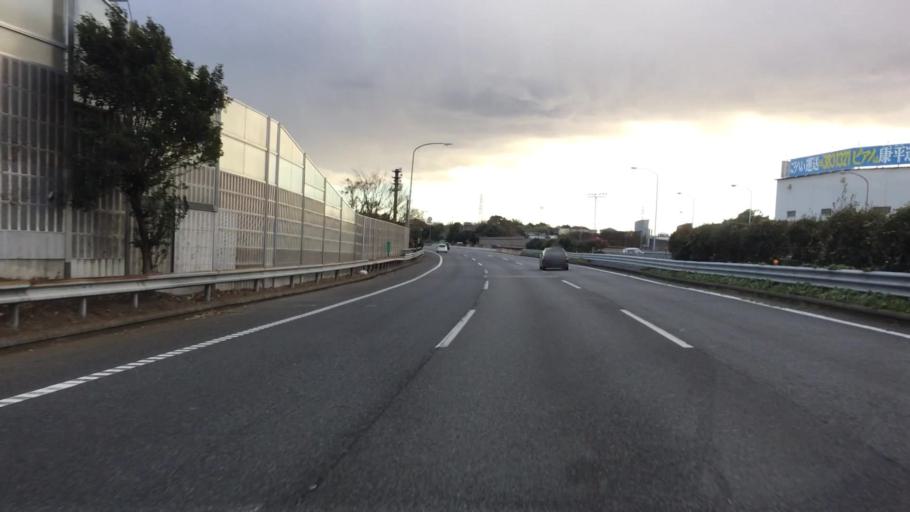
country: JP
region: Kanagawa
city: Yokohama
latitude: 35.4883
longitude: 139.5924
